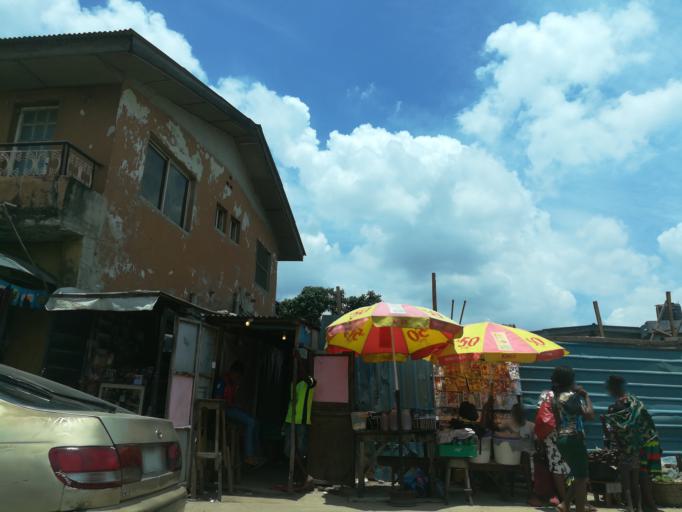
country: NG
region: Lagos
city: Ebute Ikorodu
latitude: 6.6028
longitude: 3.4903
